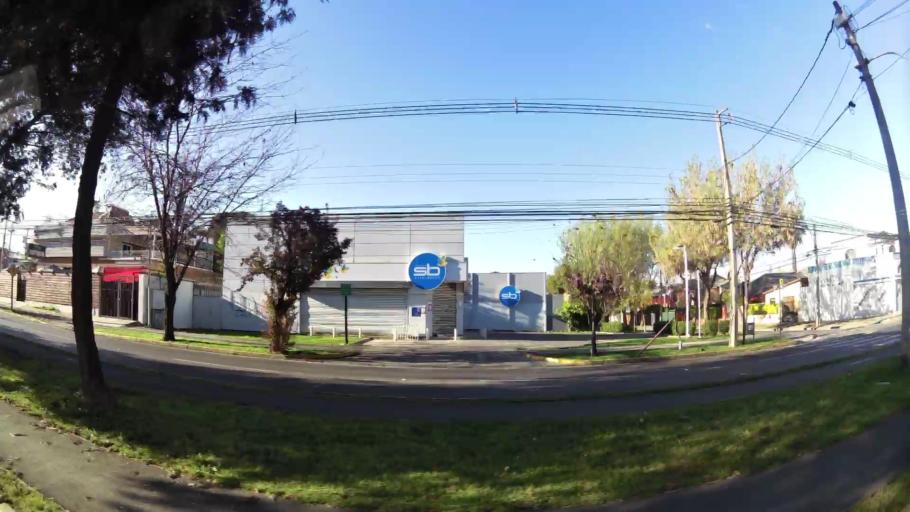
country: CL
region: Santiago Metropolitan
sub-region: Provincia de Santiago
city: Villa Presidente Frei, Nunoa, Santiago, Chile
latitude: -33.4525
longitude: -70.5622
